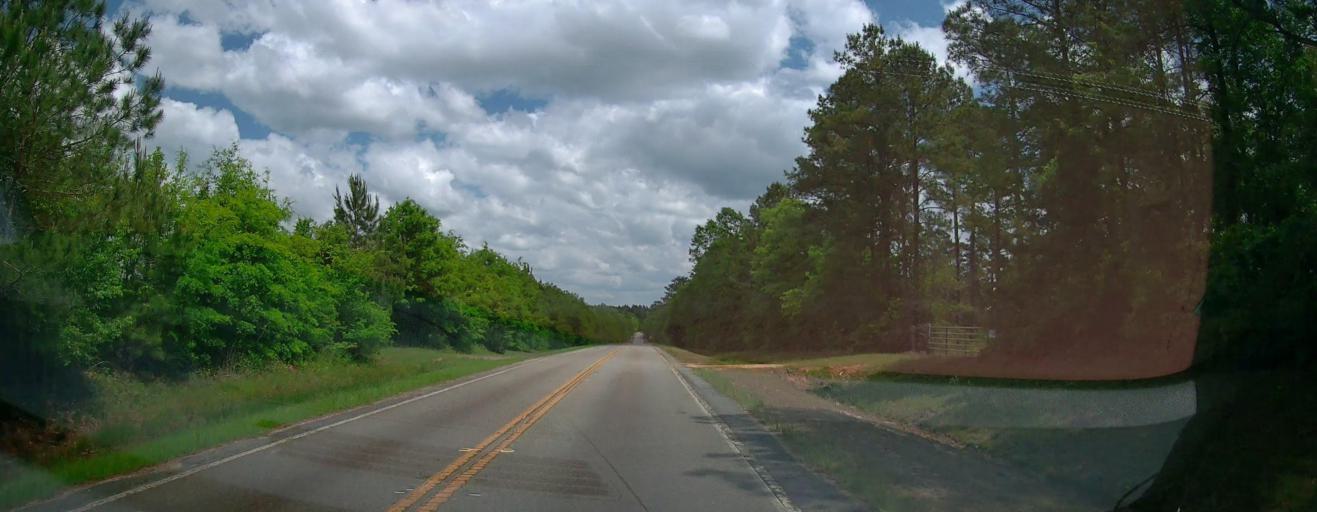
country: US
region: Georgia
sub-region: Dodge County
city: Chester
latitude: 32.5310
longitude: -83.2041
